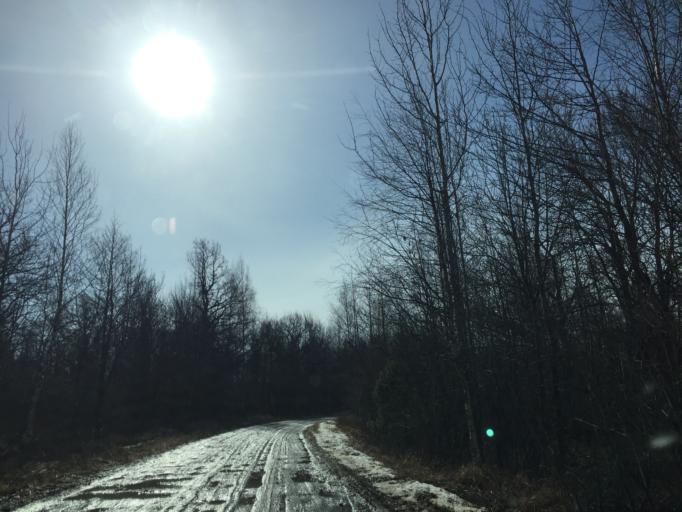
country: EE
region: Laeaene
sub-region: Haapsalu linn
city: Haapsalu
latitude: 58.6567
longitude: 23.5143
